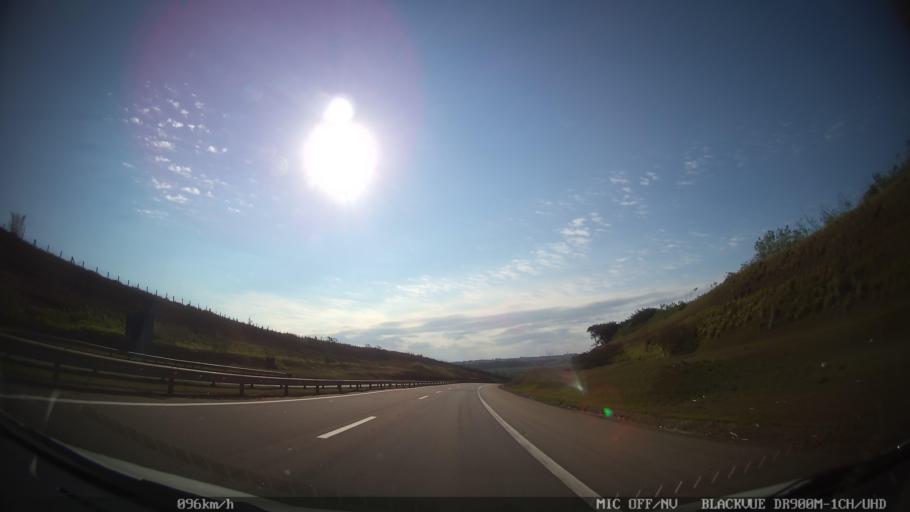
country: BR
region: Sao Paulo
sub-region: Piracicaba
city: Piracicaba
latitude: -22.7096
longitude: -47.6110
